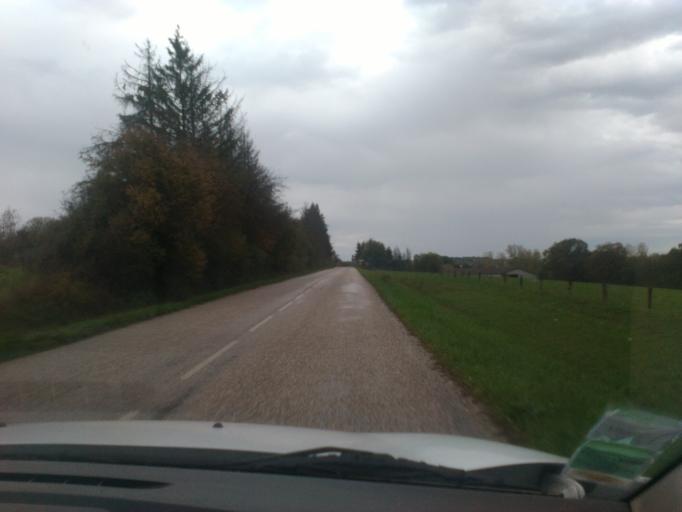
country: FR
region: Lorraine
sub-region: Departement des Vosges
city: Dogneville
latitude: 48.2721
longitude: 6.4919
